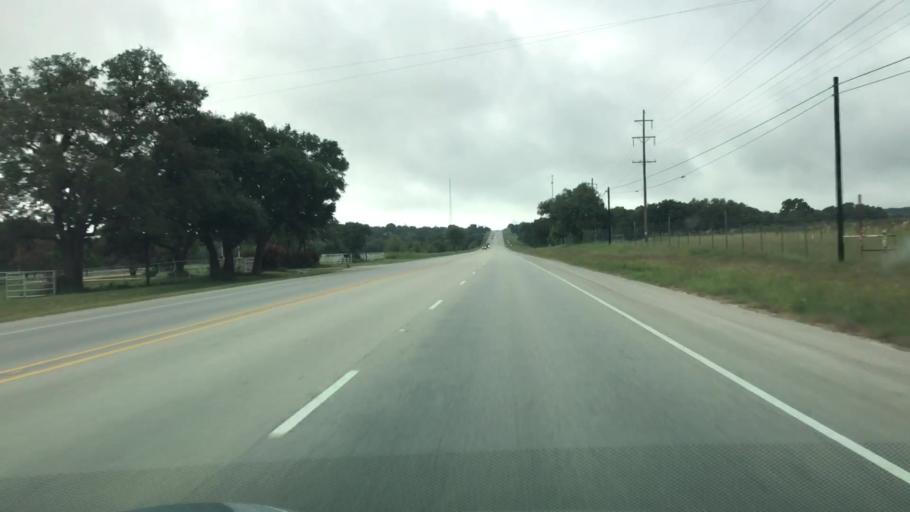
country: US
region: Texas
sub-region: Blanco County
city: Blanco
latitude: 30.0613
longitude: -98.4112
